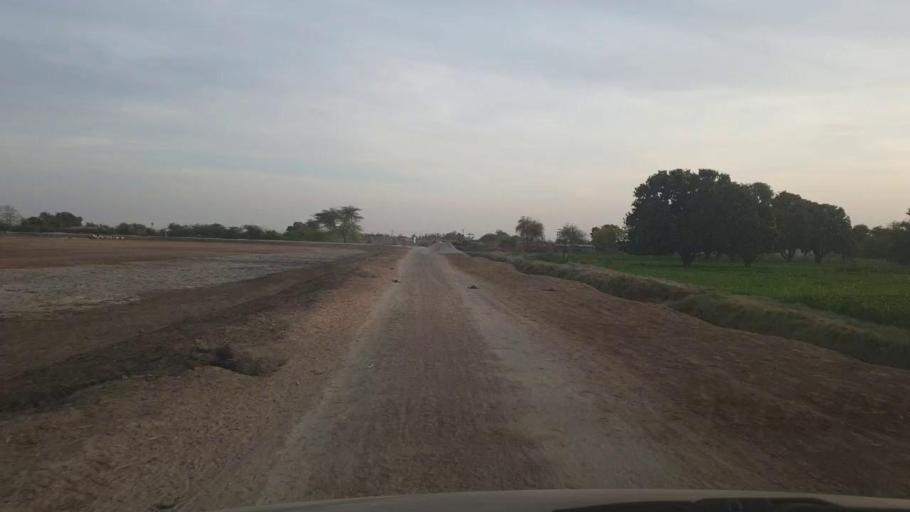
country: PK
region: Sindh
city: Kunri
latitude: 25.2144
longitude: 69.5740
